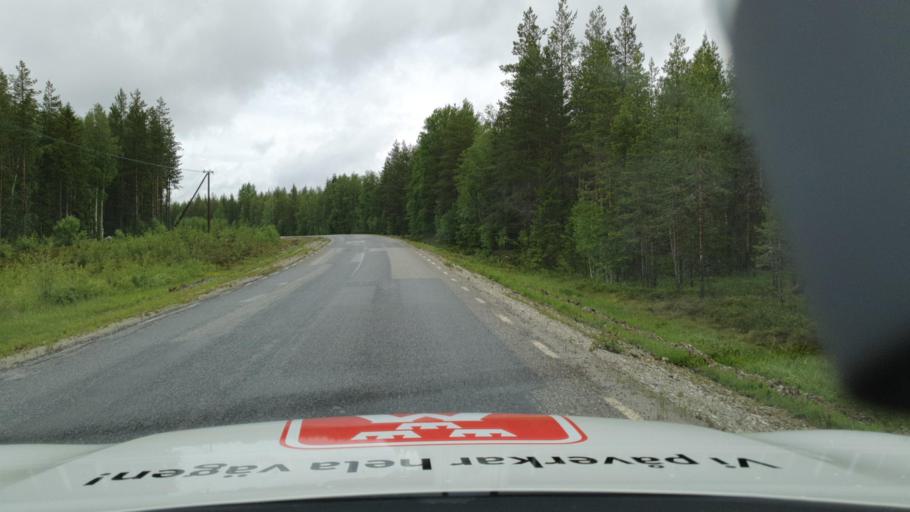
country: SE
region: Vaesterbotten
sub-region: Dorotea Kommun
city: Dorotea
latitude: 64.1429
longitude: 16.6457
